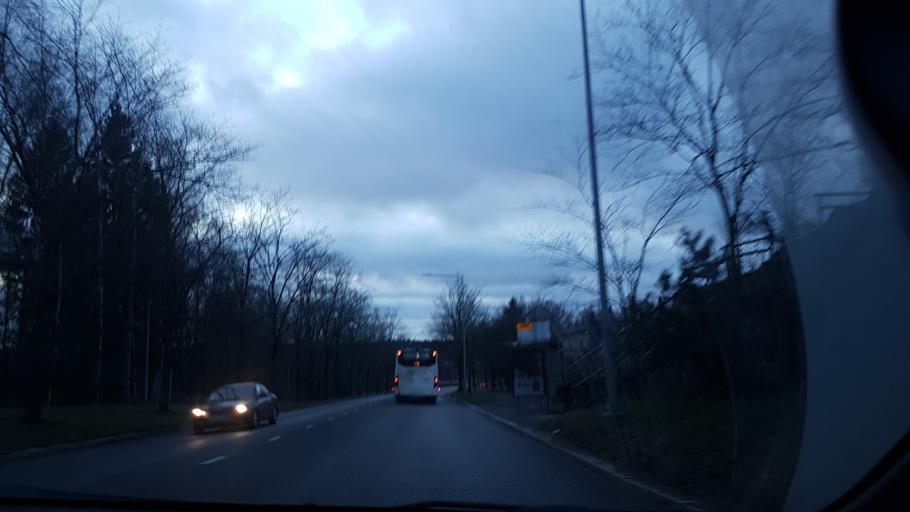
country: FI
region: Uusimaa
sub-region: Helsinki
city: Vantaa
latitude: 60.2729
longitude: 25.1042
